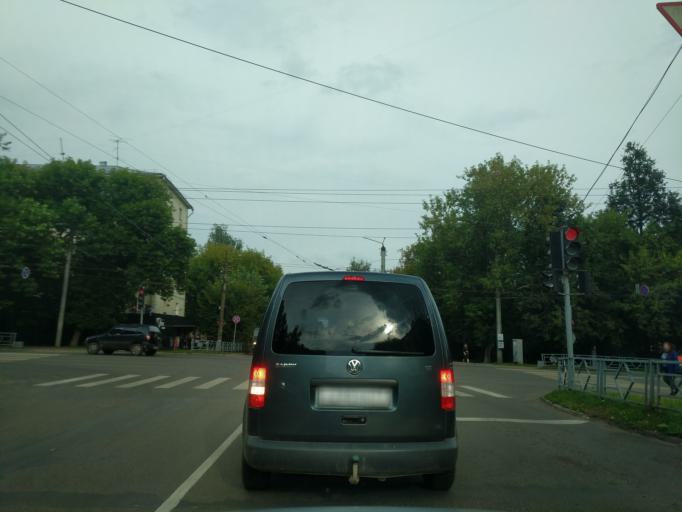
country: RU
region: Kirov
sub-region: Kirovo-Chepetskiy Rayon
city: Kirov
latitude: 58.5872
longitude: 49.6693
